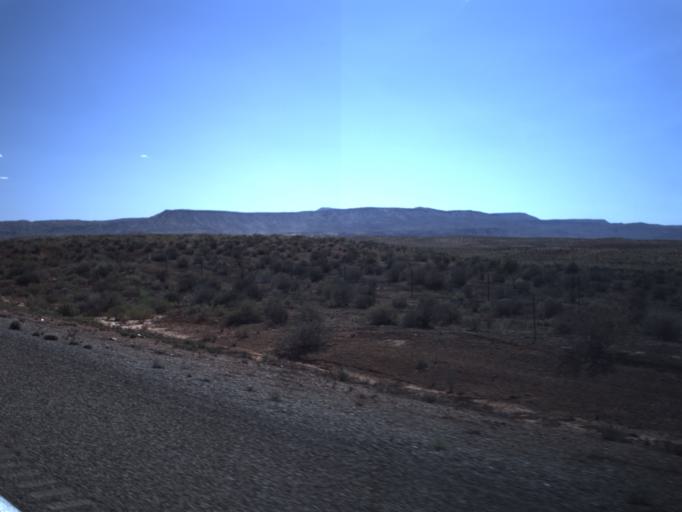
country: US
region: Utah
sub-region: Washington County
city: Saint George
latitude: 37.0030
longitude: -113.5811
